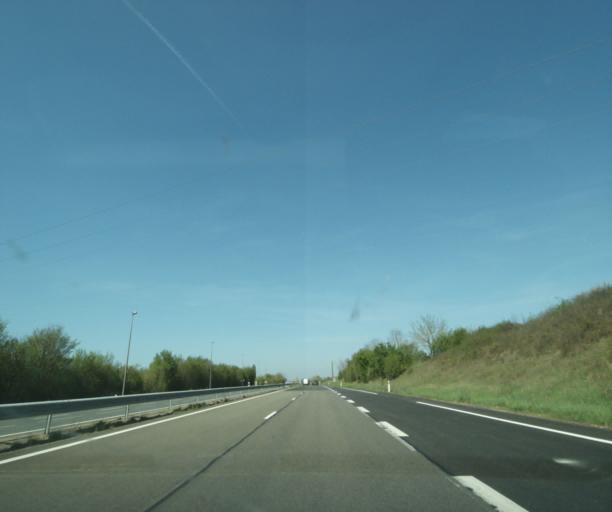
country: FR
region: Bourgogne
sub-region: Departement de la Nievre
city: La Charite-sur-Loire
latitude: 47.1885
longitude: 3.0339
